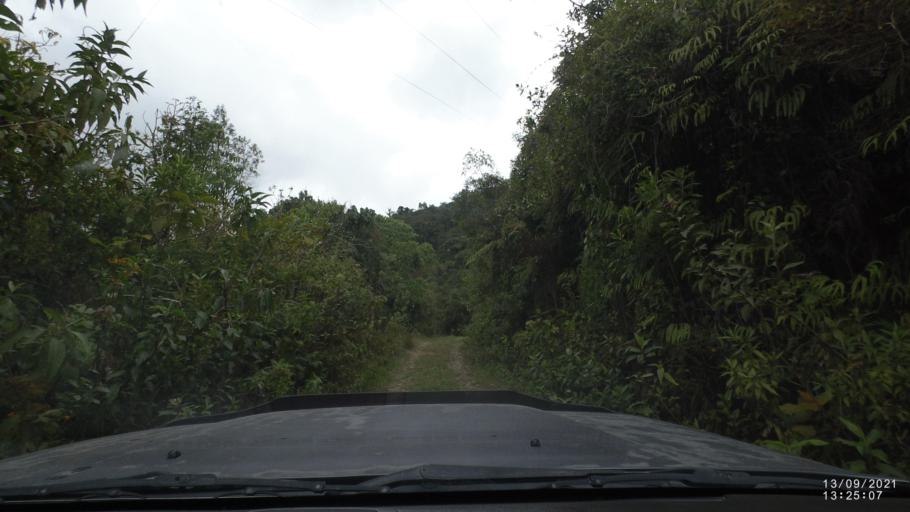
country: BO
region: Cochabamba
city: Colomi
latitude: -17.2117
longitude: -65.8654
